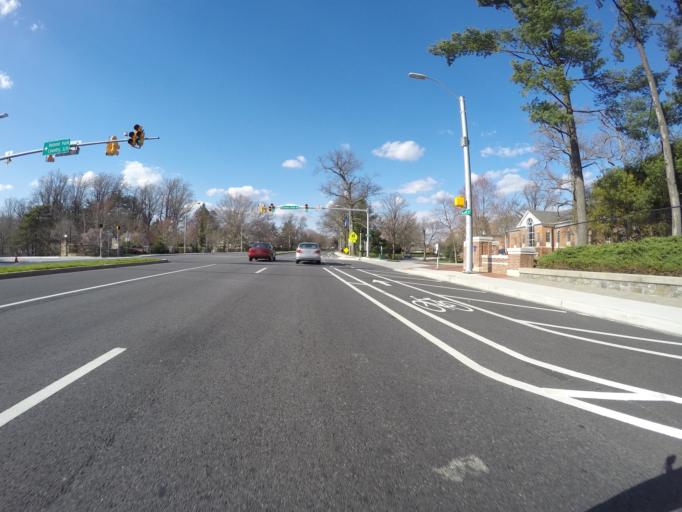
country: US
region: Maryland
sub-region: Baltimore County
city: Towson
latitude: 39.3577
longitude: -76.6349
